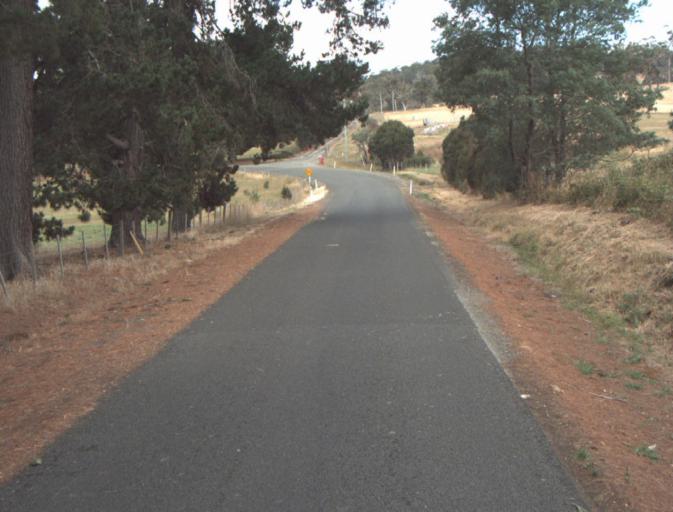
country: AU
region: Tasmania
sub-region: Launceston
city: Mayfield
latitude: -41.2938
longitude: 147.0076
